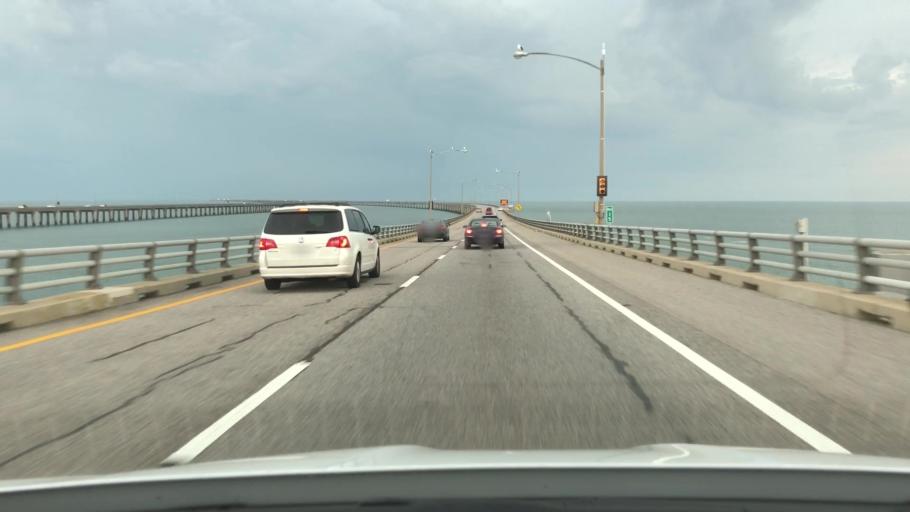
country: US
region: Virginia
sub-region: Northampton County
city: Cape Charles
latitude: 37.0890
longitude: -75.9951
